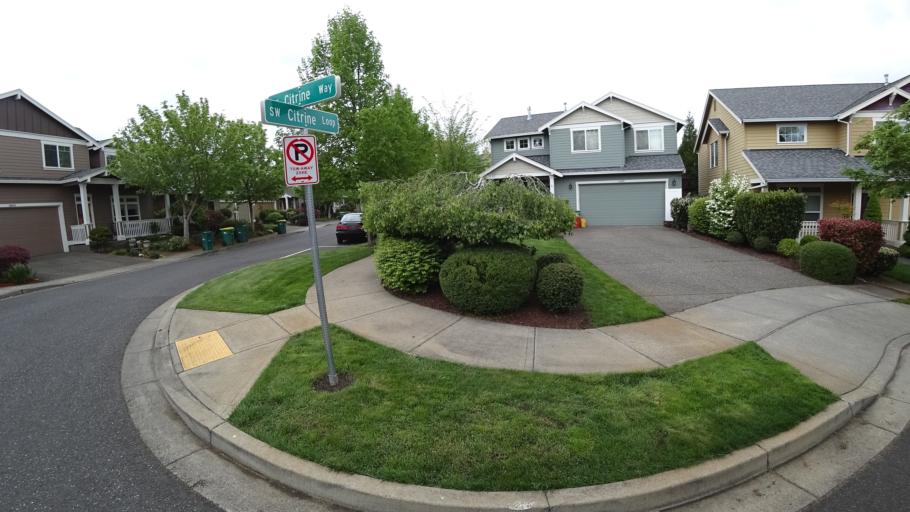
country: US
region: Oregon
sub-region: Washington County
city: Beaverton
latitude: 45.4575
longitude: -122.8286
